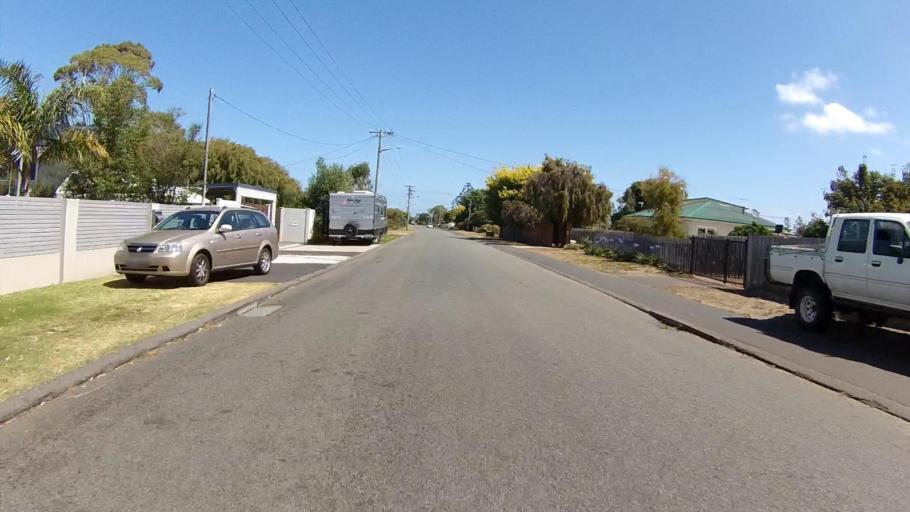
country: AU
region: Tasmania
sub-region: Clarence
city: Lauderdale
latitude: -42.9001
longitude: 147.4961
